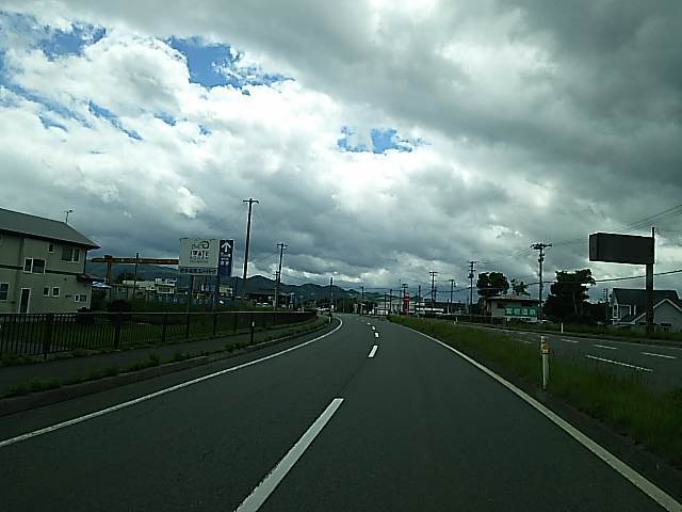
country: JP
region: Iwate
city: Morioka-shi
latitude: 39.7086
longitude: 141.0901
